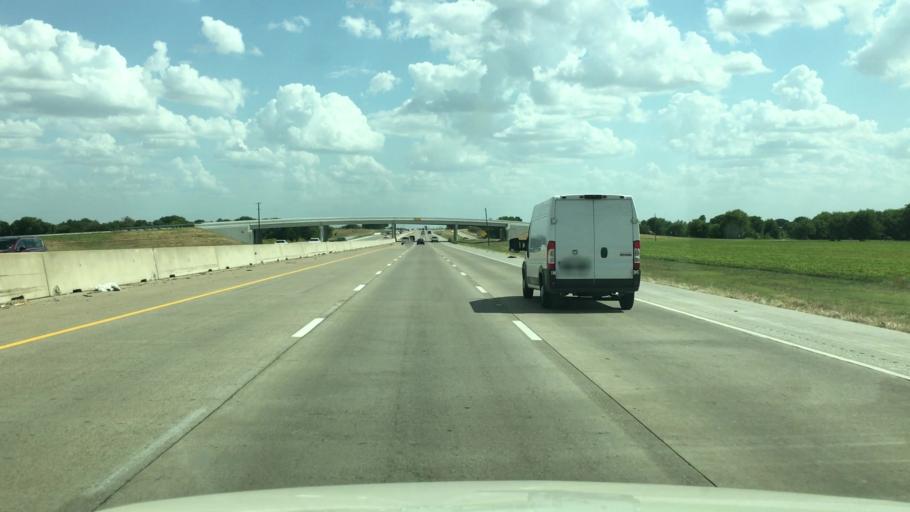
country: US
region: Texas
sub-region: Ellis County
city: Nash
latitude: 32.2928
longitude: -96.8663
